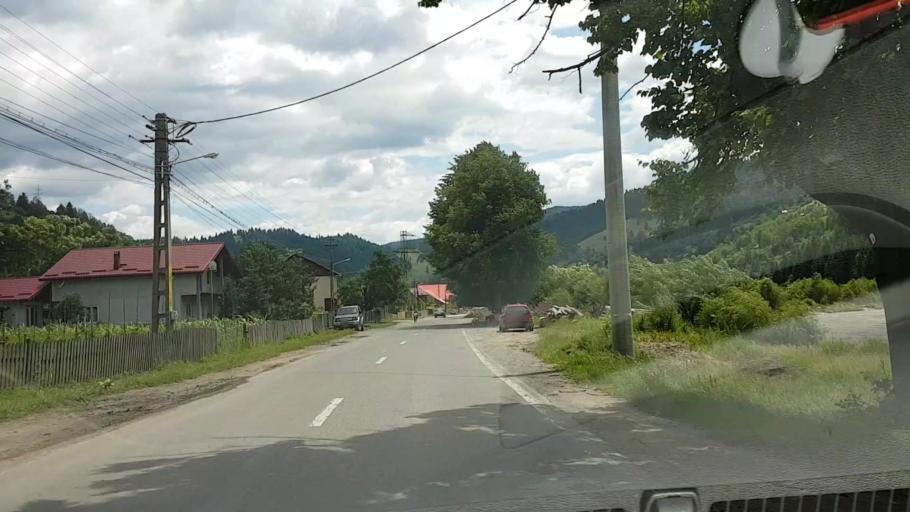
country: RO
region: Suceava
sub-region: Comuna Brosteni
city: Brosteni
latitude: 47.2411
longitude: 25.7078
